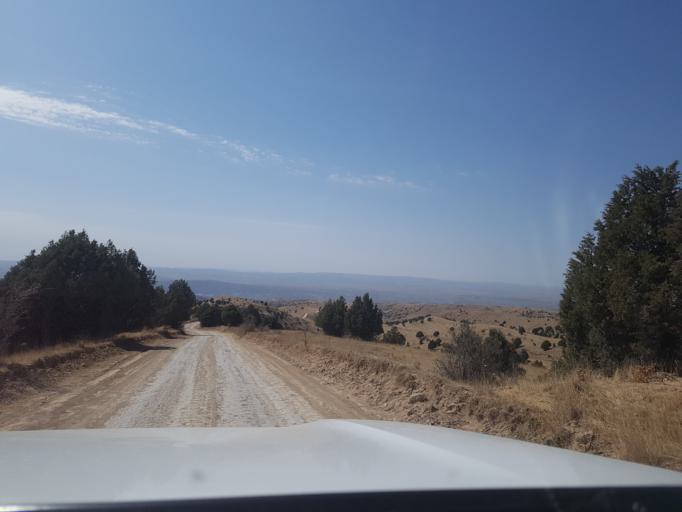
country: TM
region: Ahal
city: Baharly
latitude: 38.3110
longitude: 56.9503
